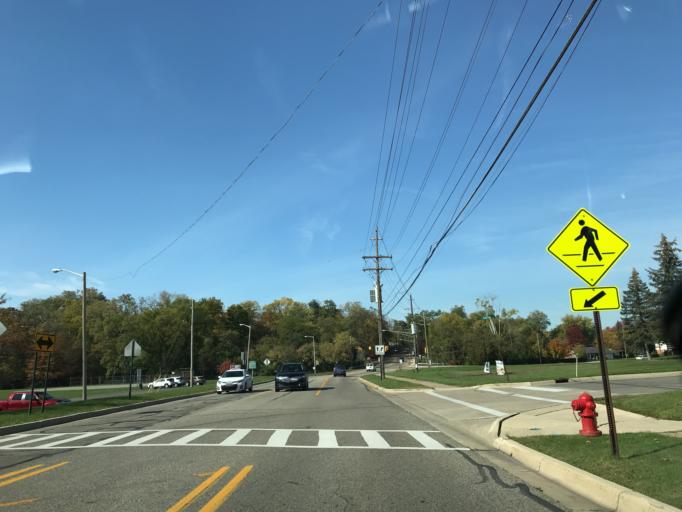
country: US
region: Michigan
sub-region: Oakland County
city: Farmington
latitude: 42.4658
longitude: -83.3692
